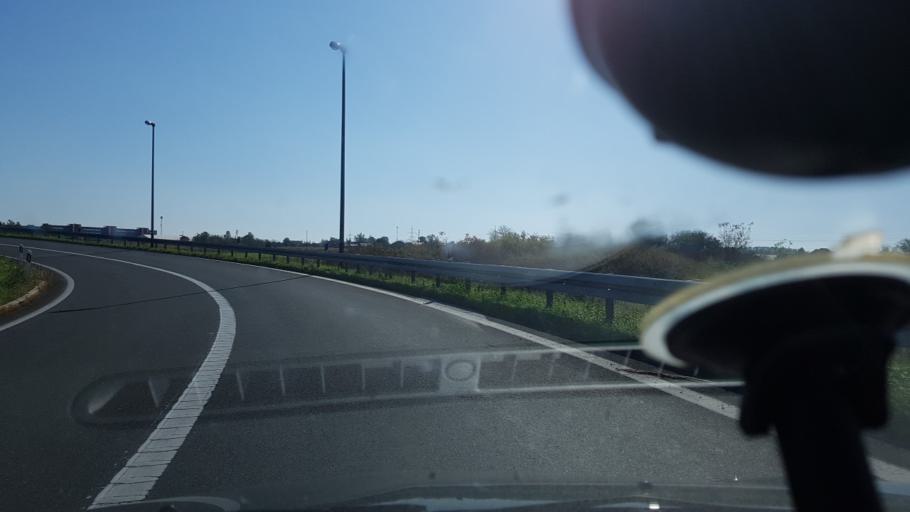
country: HR
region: Zagrebacka
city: Brckovljani
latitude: 45.7636
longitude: 16.2238
